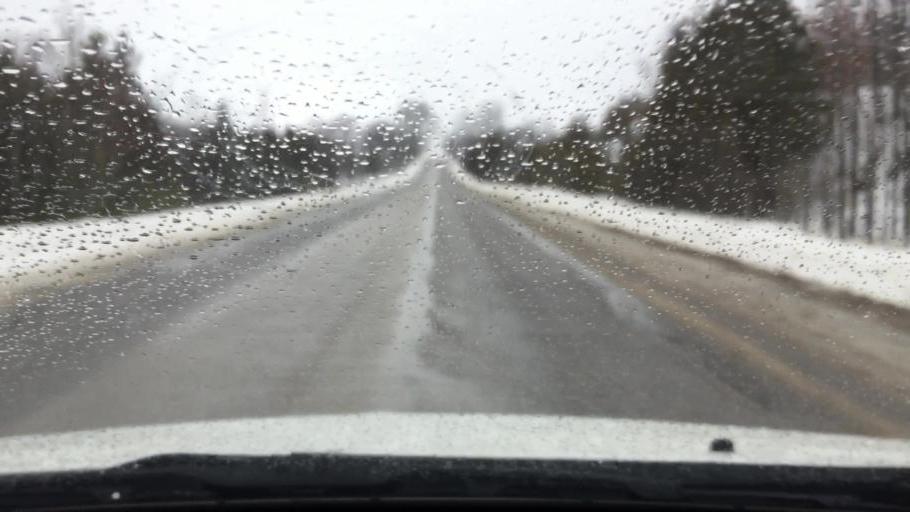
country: US
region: Michigan
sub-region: Charlevoix County
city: East Jordan
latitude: 45.1325
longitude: -85.1500
